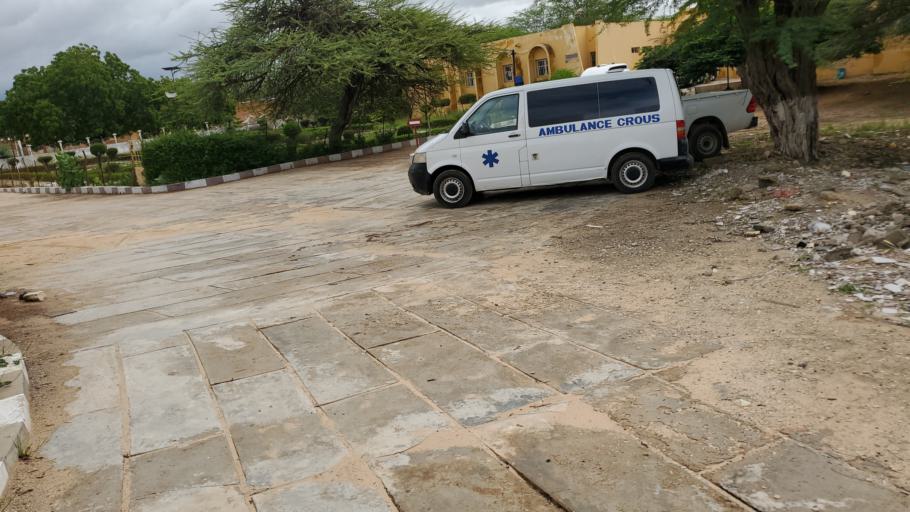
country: SN
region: Saint-Louis
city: Saint-Louis
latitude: 16.0671
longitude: -16.4263
